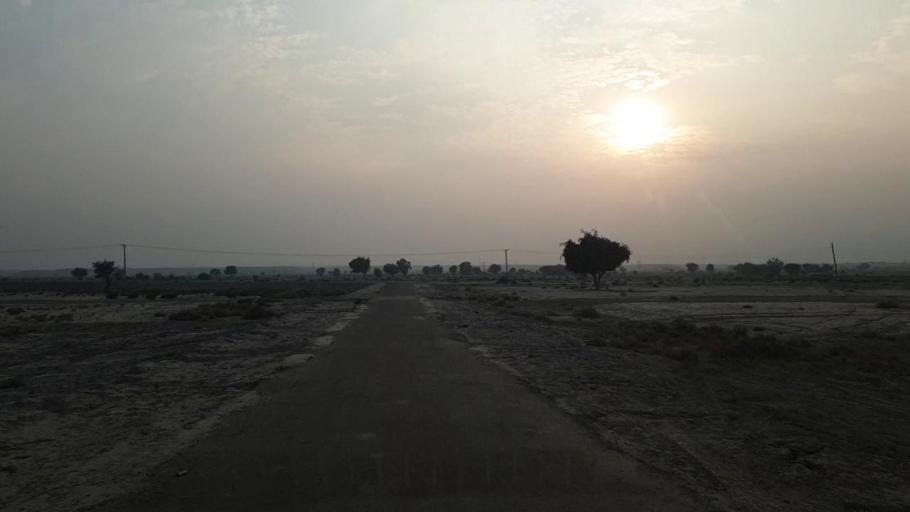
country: PK
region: Sindh
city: Sann
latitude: 26.1792
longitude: 67.9910
